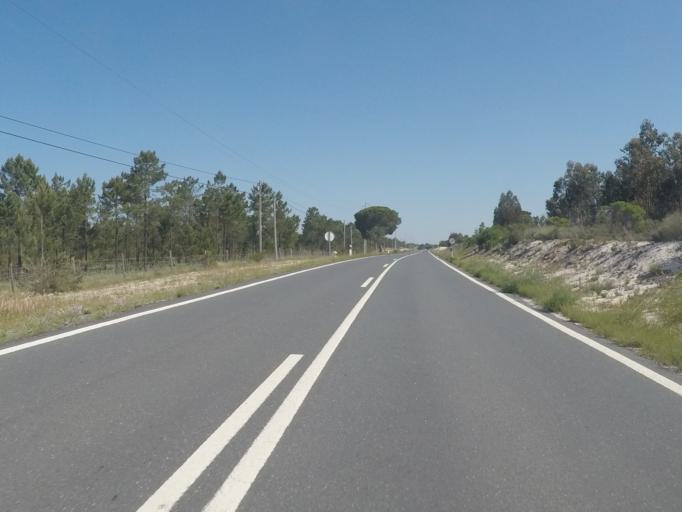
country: PT
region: Setubal
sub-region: Grandola
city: Grandola
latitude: 38.2414
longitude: -8.7373
